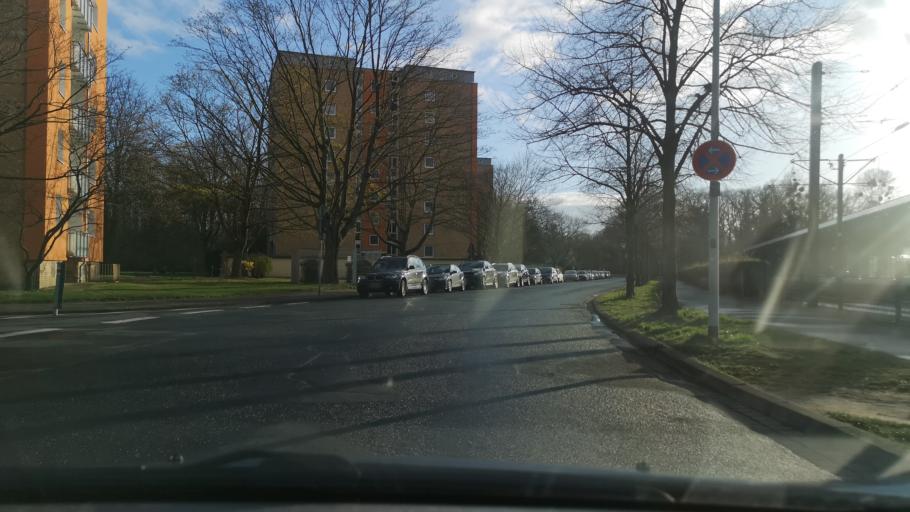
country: DE
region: Lower Saxony
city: Garbsen-Mitte
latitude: 52.4143
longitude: 9.6684
